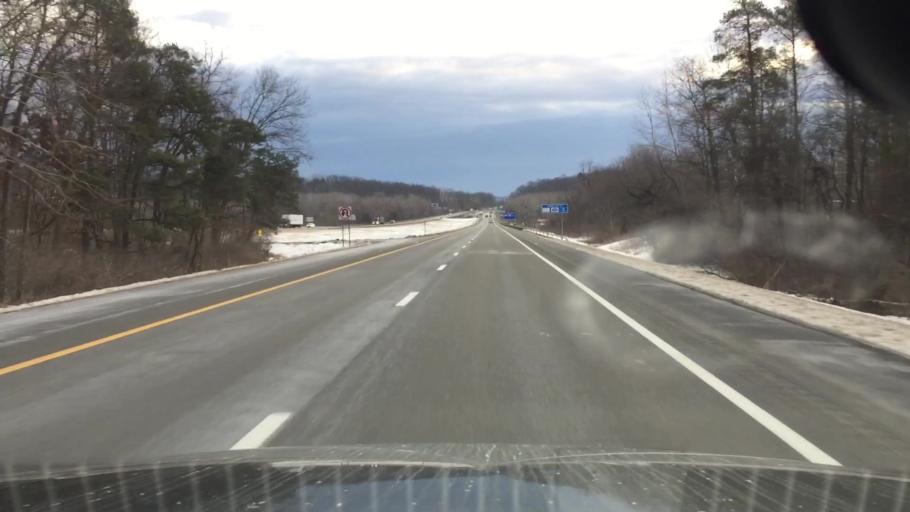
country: US
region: Pennsylvania
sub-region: Bradford County
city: South Waverly
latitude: 42.0005
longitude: -76.5688
